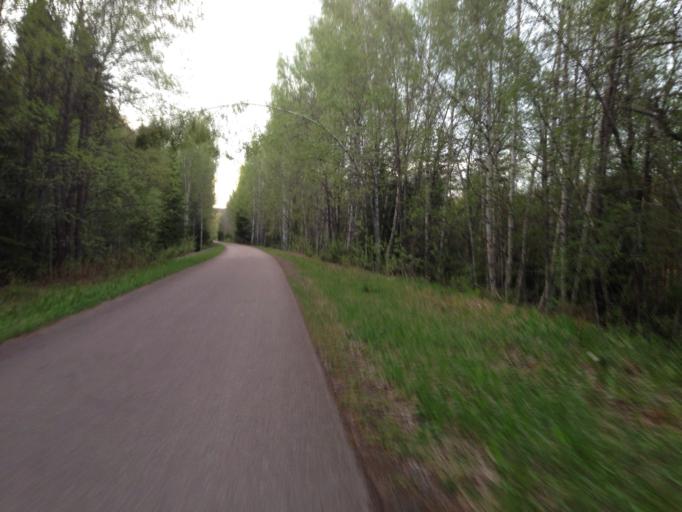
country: SE
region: Dalarna
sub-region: Ludvika Kommun
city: Grangesberg
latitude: 60.1262
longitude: 15.0700
